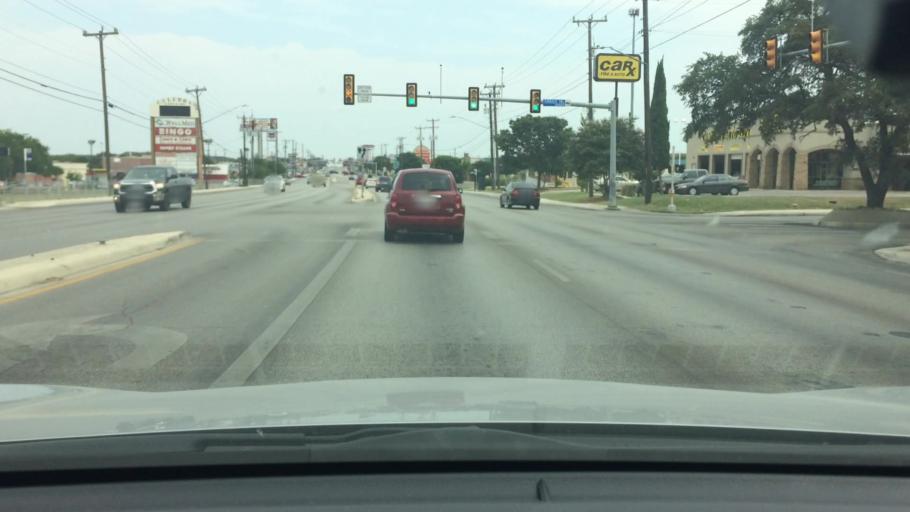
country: US
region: Texas
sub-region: Bexar County
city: Leon Valley
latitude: 29.4698
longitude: -98.6505
